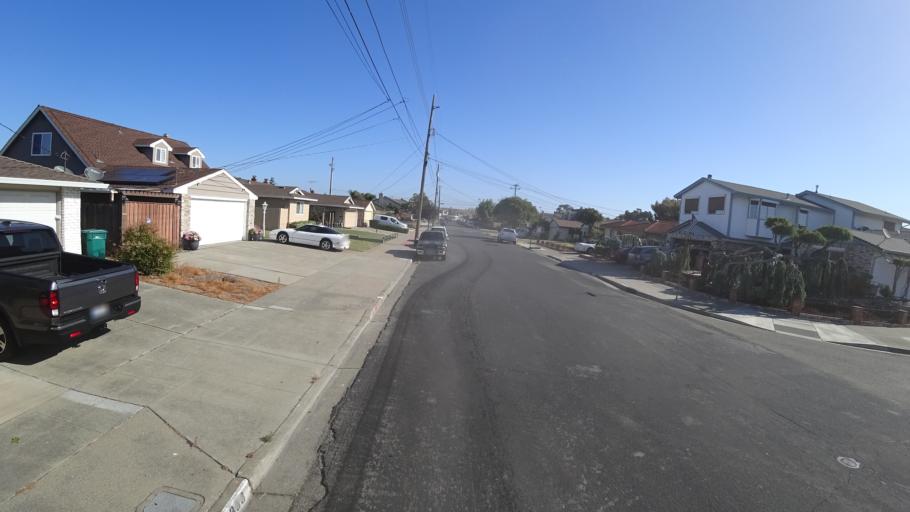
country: US
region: California
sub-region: Alameda County
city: Hayward
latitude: 37.6189
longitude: -122.0919
